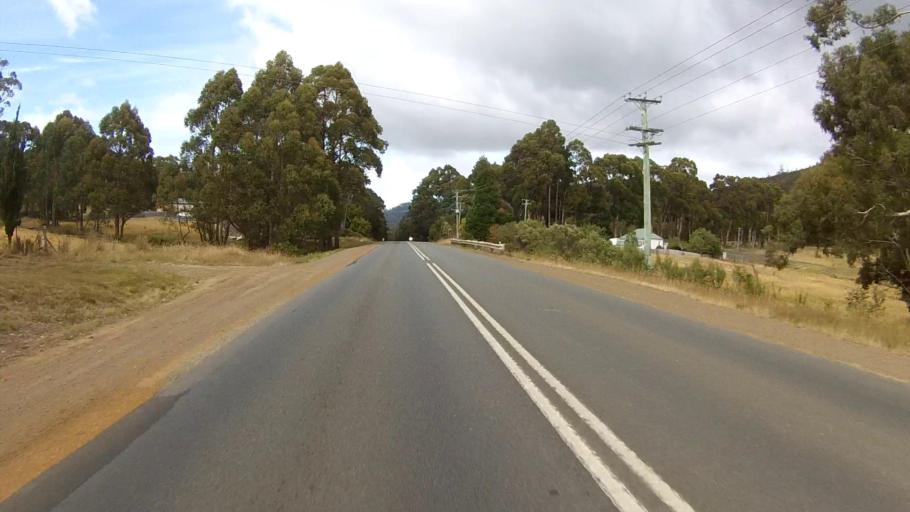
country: AU
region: Tasmania
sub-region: Kingborough
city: Kettering
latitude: -43.0932
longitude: 147.2460
